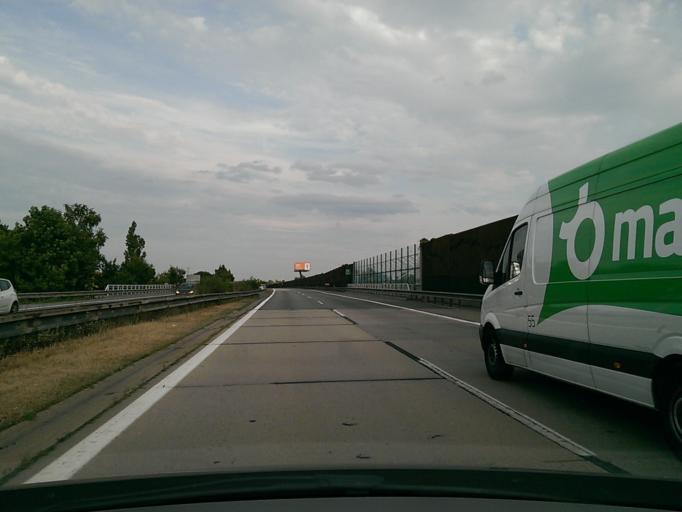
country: CZ
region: Vysocina
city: Merin
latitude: 49.3934
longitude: 15.8954
